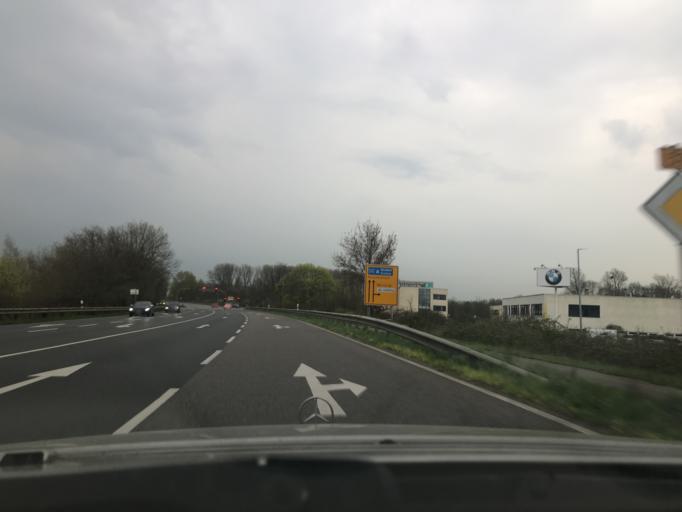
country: DE
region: North Rhine-Westphalia
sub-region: Regierungsbezirk Dusseldorf
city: Korschenbroich
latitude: 51.2228
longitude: 6.4838
